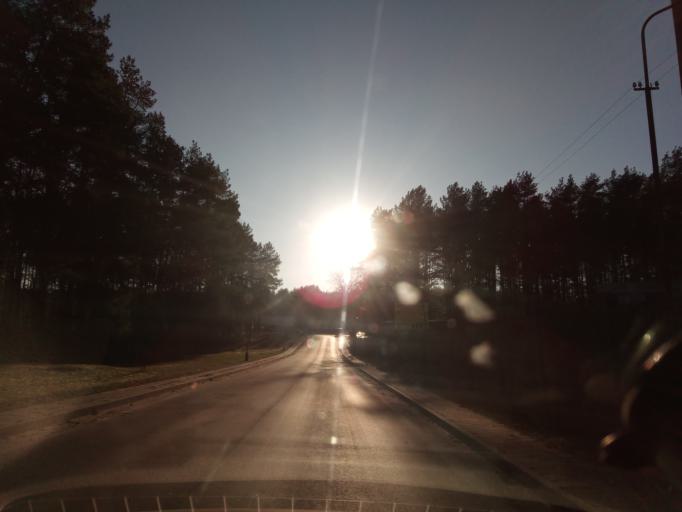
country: LT
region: Alytaus apskritis
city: Druskininkai
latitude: 54.0039
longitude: 23.9803
